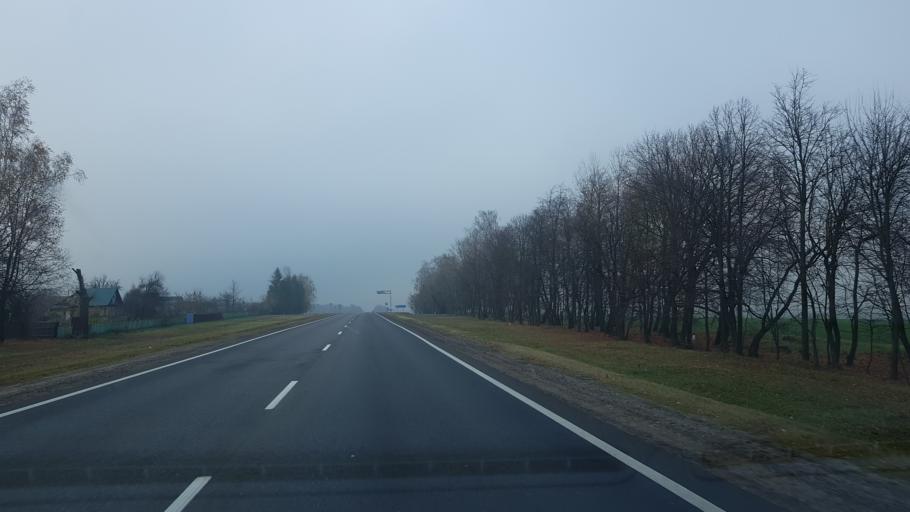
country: BY
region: Mogilev
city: Babruysk
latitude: 53.1791
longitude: 29.3482
